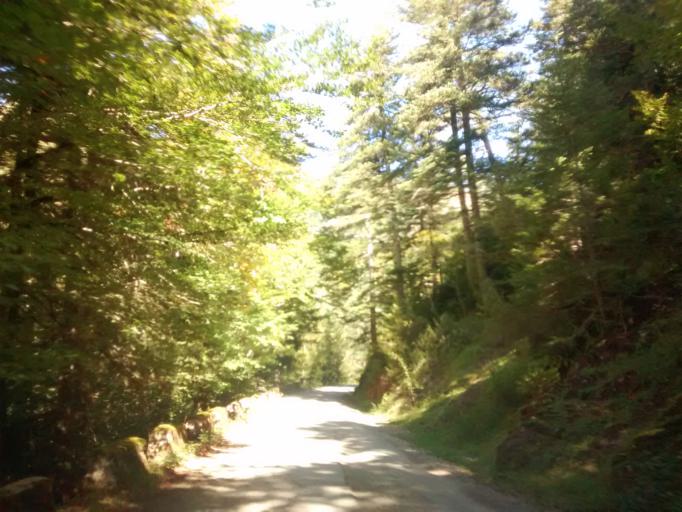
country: ES
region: Aragon
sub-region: Provincia de Huesca
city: Aragues del Puerto
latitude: 42.8410
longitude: -0.7109
